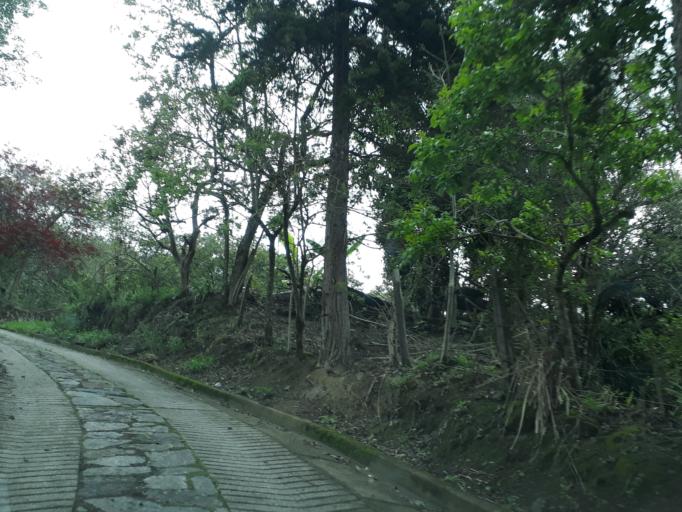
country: CO
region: Cundinamarca
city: Manta
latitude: 5.0015
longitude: -73.5345
